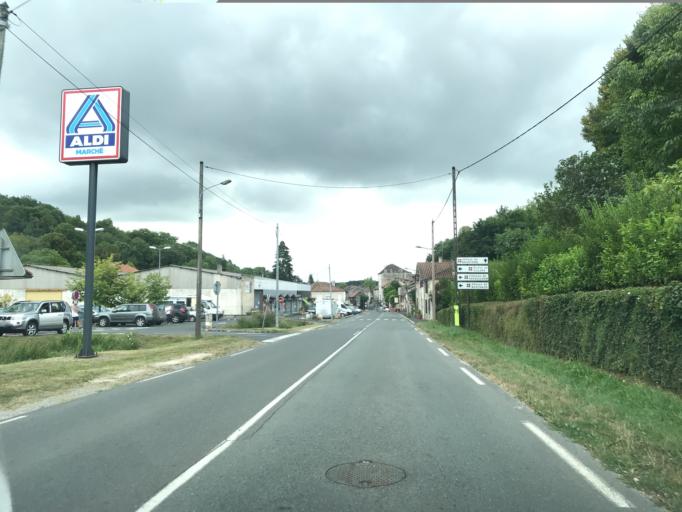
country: FR
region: Aquitaine
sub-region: Departement de la Dordogne
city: Brantome
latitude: 45.3690
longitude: 0.6474
